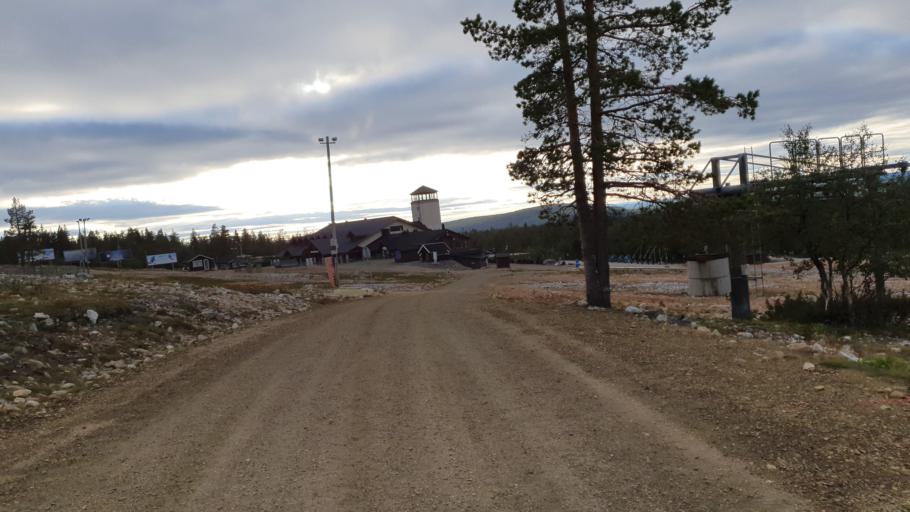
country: FI
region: Lapland
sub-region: Tunturi-Lappi
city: Kolari
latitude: 67.5796
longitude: 24.2080
